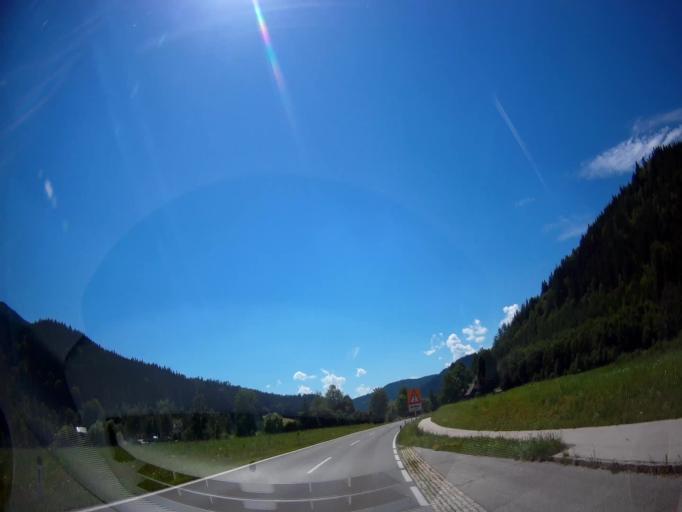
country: AT
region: Carinthia
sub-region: Politischer Bezirk Sankt Veit an der Glan
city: Gurk
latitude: 46.8643
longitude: 14.2514
